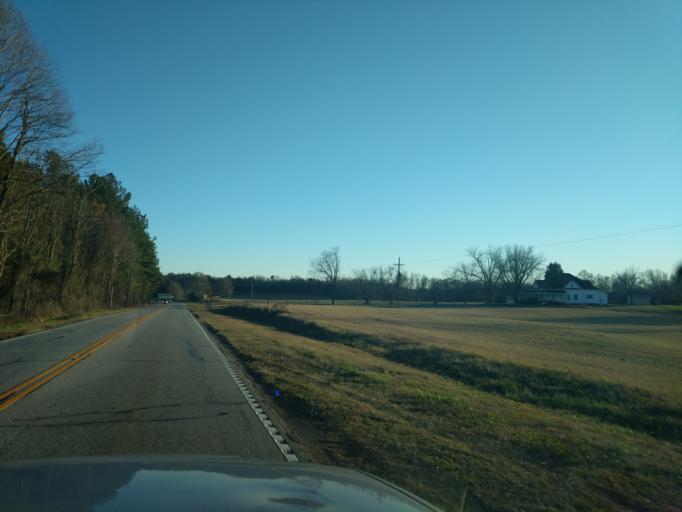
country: US
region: Georgia
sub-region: Hart County
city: Reed Creek
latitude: 34.5565
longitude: -82.8694
